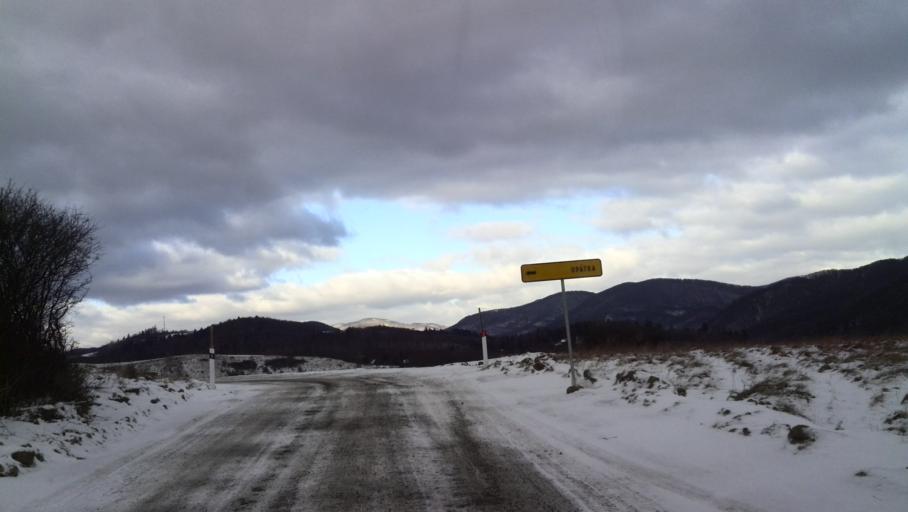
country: SK
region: Kosicky
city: Gelnica
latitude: 48.8221
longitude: 21.0725
